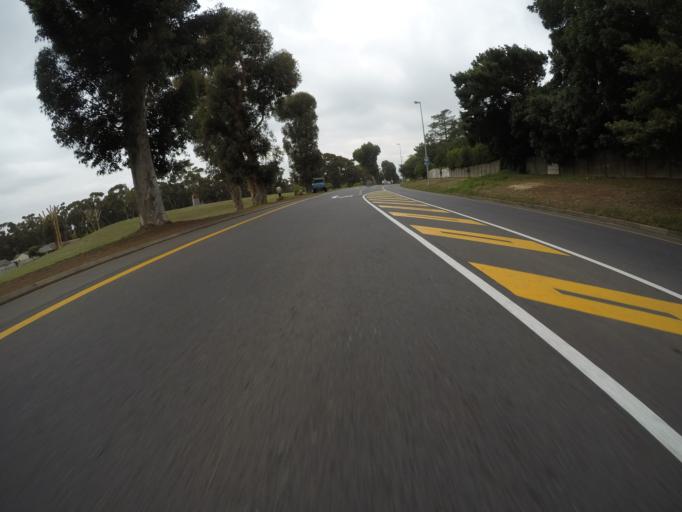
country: ZA
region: Western Cape
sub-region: City of Cape Town
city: Kraaifontein
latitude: -33.8429
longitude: 18.6379
